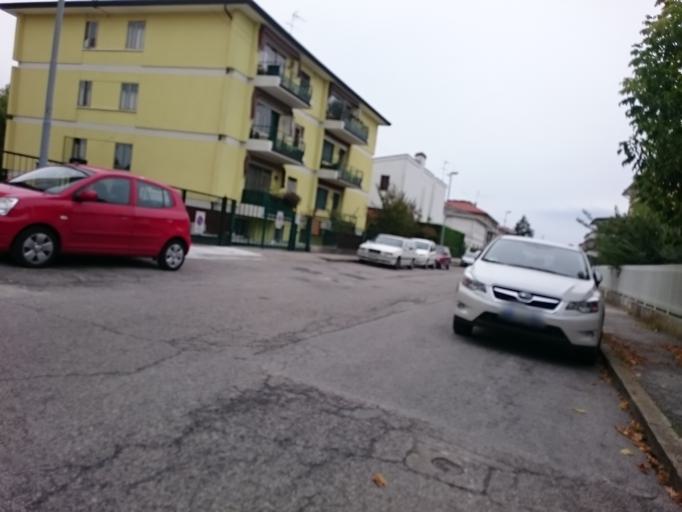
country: IT
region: Veneto
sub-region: Provincia di Padova
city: Padova
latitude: 45.3834
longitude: 11.8813
